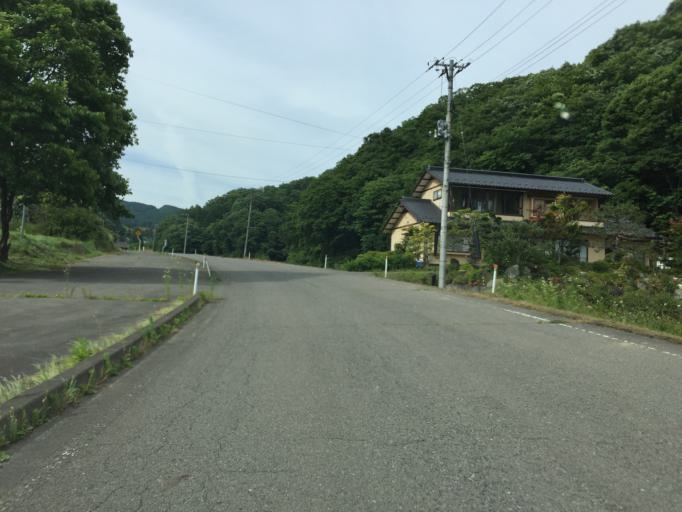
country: JP
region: Fukushima
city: Funehikimachi-funehiki
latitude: 37.4486
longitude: 140.6406
